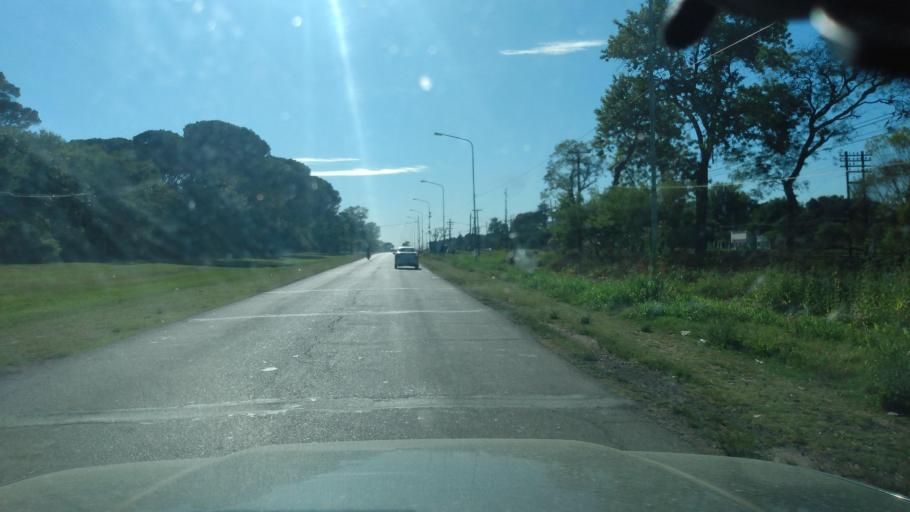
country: AR
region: Buenos Aires
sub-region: Partido de Lujan
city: Lujan
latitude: -34.5836
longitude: -59.0597
